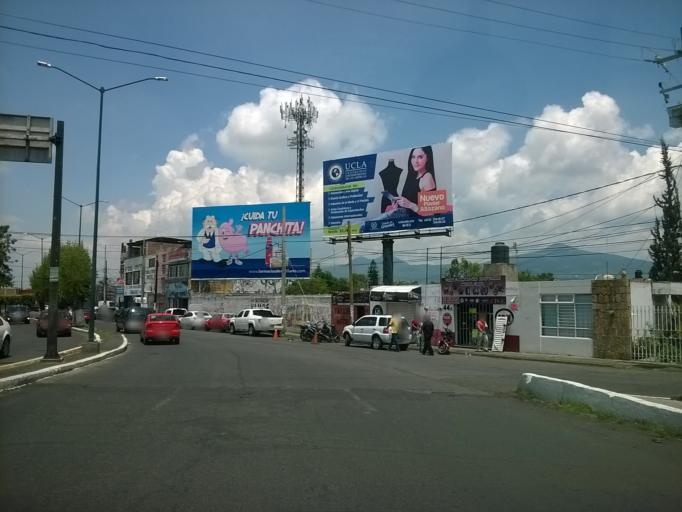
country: MX
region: Michoacan
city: Morelia
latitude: 19.7109
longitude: -101.1888
